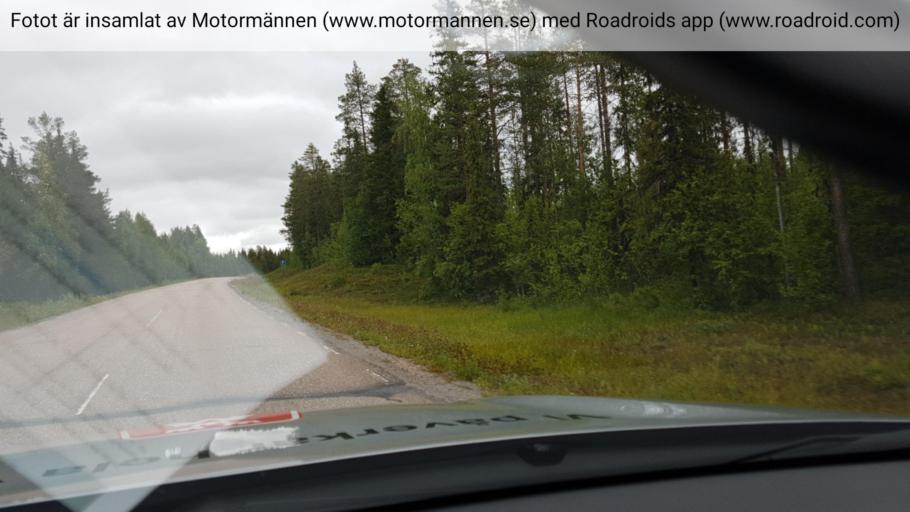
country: SE
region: Norrbotten
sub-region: Overkalix Kommun
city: OEverkalix
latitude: 67.0271
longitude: 22.0053
